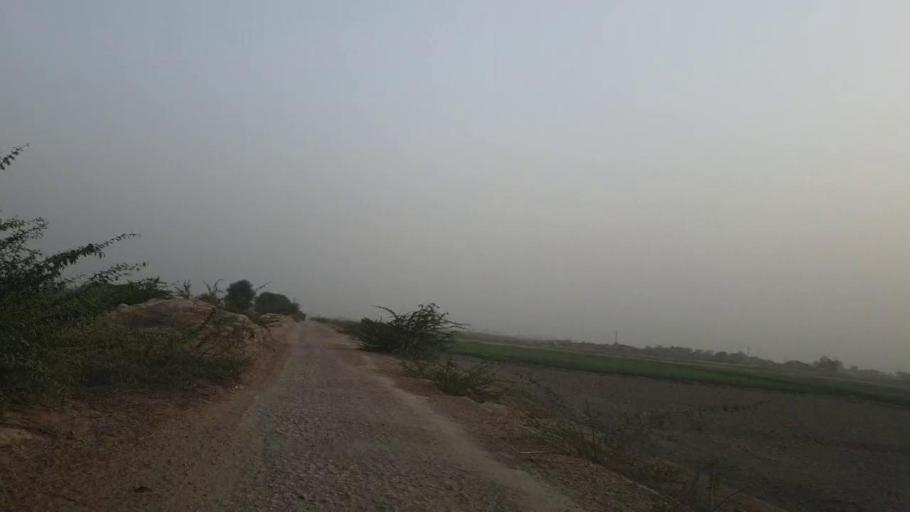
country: PK
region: Sindh
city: Kunri
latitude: 25.1163
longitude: 69.5520
